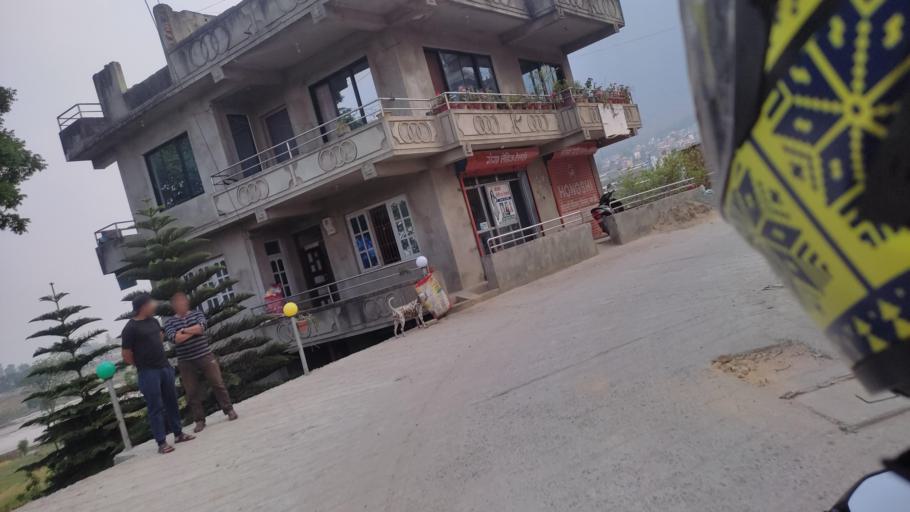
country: NP
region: Central Region
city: Kirtipur
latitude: 27.6760
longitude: 85.2537
